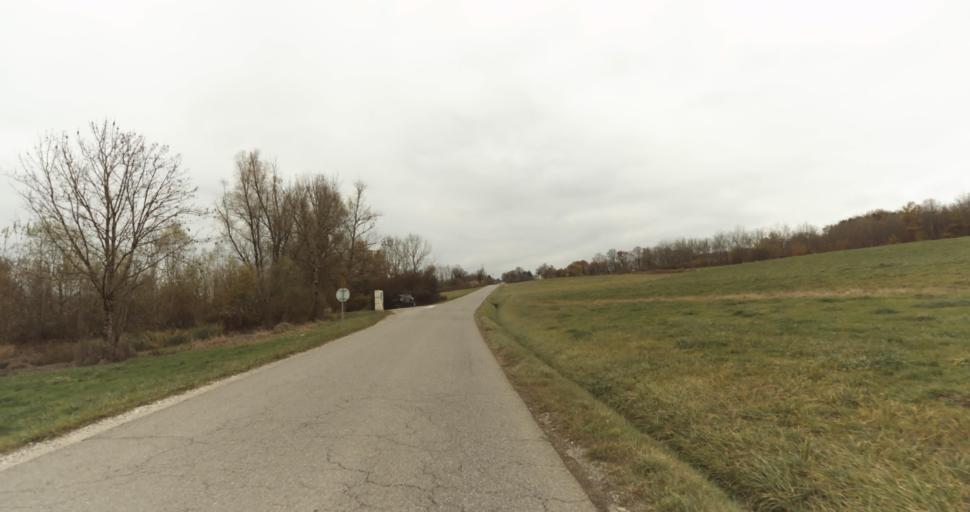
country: FR
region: Rhone-Alpes
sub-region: Departement de la Haute-Savoie
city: Allonzier-la-Caille
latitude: 45.9828
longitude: 6.1263
